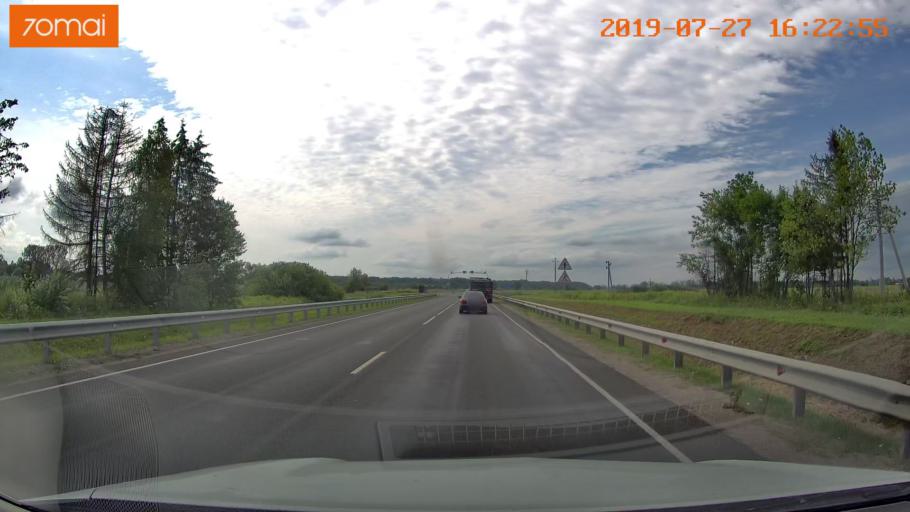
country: RU
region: Kaliningrad
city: Zheleznodorozhnyy
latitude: 54.6296
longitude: 21.4844
